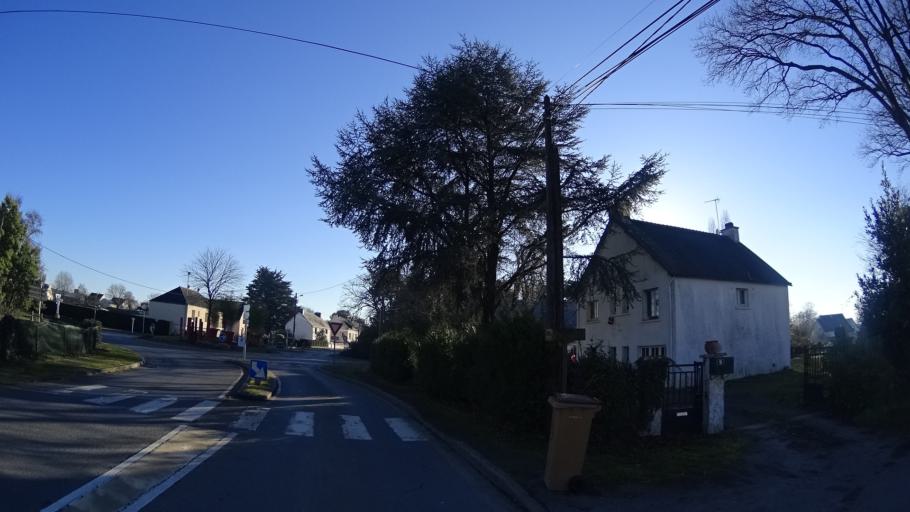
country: FR
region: Brittany
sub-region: Departement du Morbihan
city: Allaire
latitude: 47.6410
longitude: -2.1653
